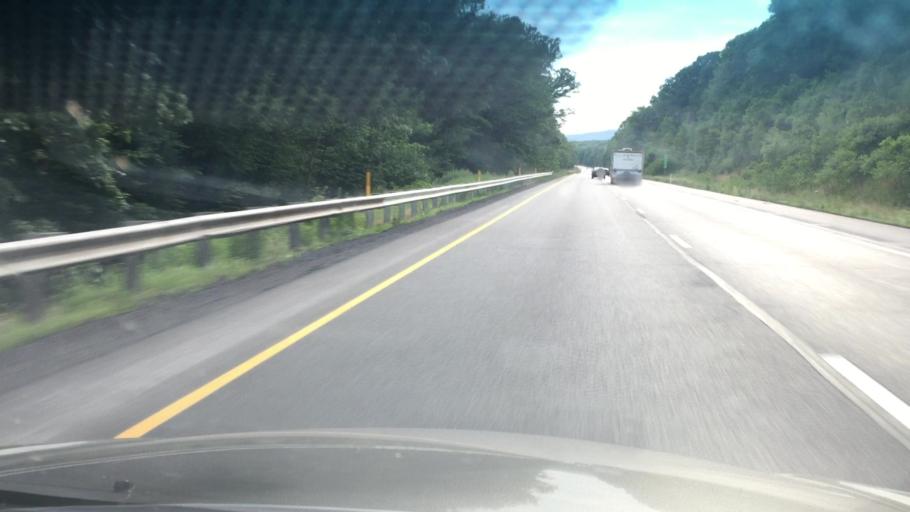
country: US
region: Pennsylvania
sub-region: Luzerne County
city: Freeland
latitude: 41.0615
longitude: -75.8876
